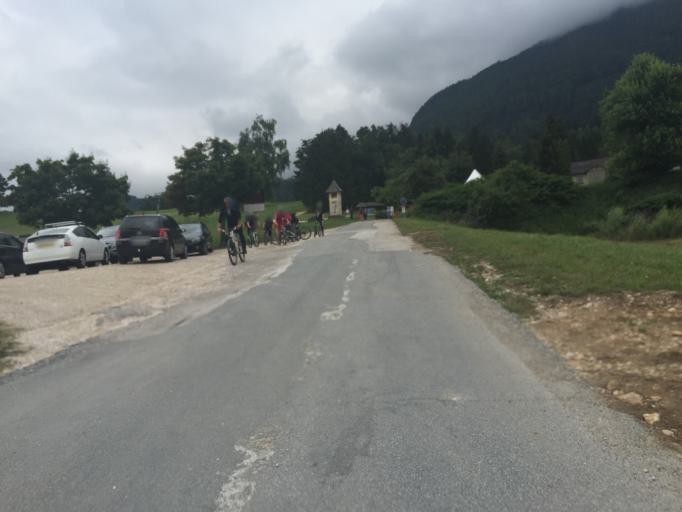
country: AT
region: Carinthia
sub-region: Politischer Bezirk Volkermarkt
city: Feistritz ob Bleiburg
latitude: 46.5426
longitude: 14.7740
